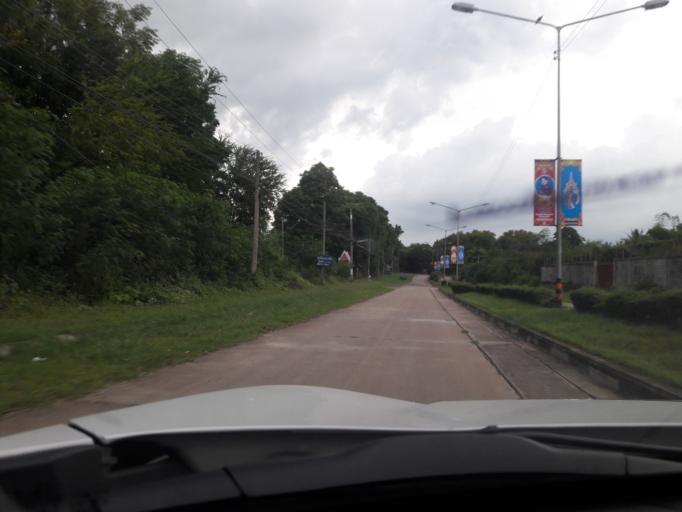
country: TH
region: Lop Buri
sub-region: Amphoe Tha Luang
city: Tha Luang
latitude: 15.0705
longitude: 101.1085
